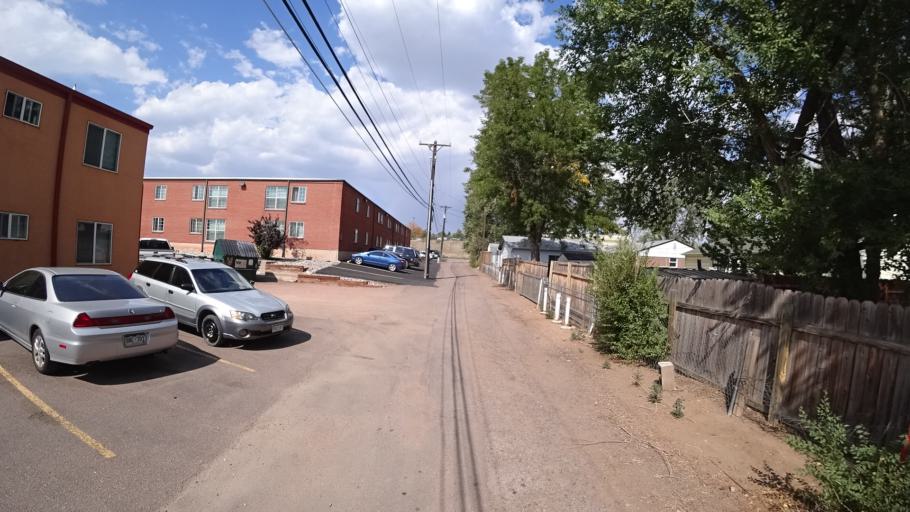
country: US
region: Colorado
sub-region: El Paso County
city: Colorado Springs
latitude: 38.8463
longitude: -104.7732
